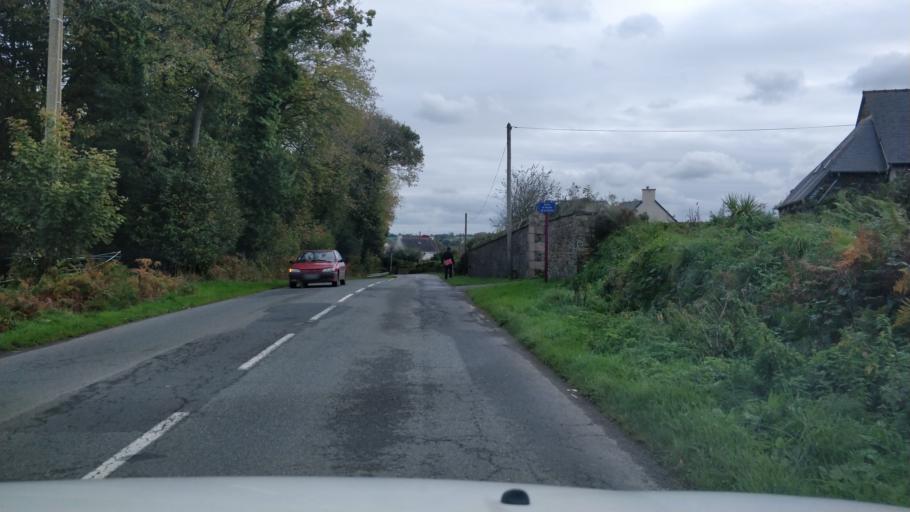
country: FR
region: Brittany
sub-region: Departement des Cotes-d'Armor
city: Langoat
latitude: 48.7506
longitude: -3.2751
